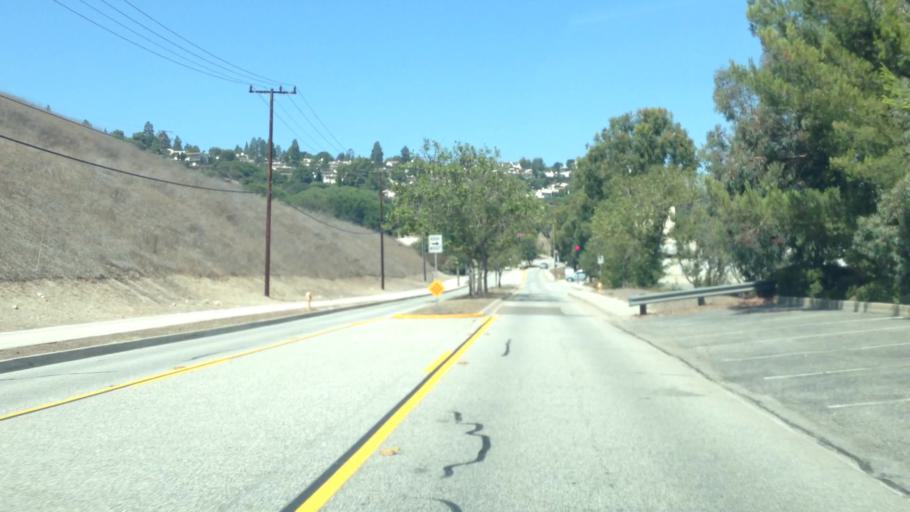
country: US
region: California
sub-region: Los Angeles County
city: Rolling Hills Estates
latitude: 33.7704
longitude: -118.3731
